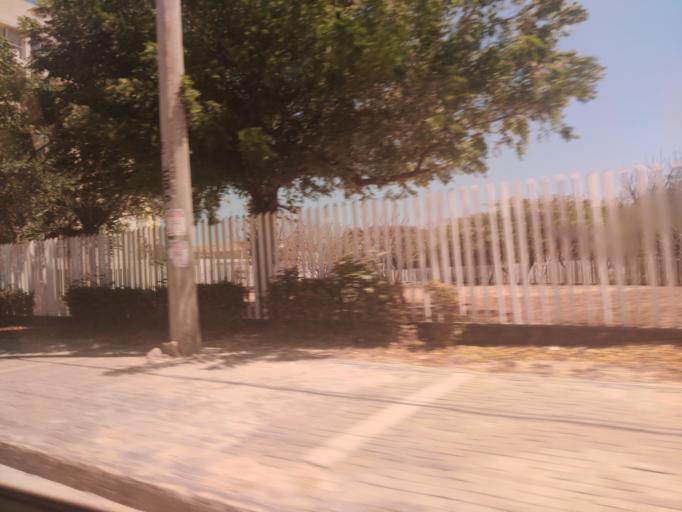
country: CO
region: Atlantico
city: Puerto Colombia
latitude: 10.9954
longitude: -74.9538
